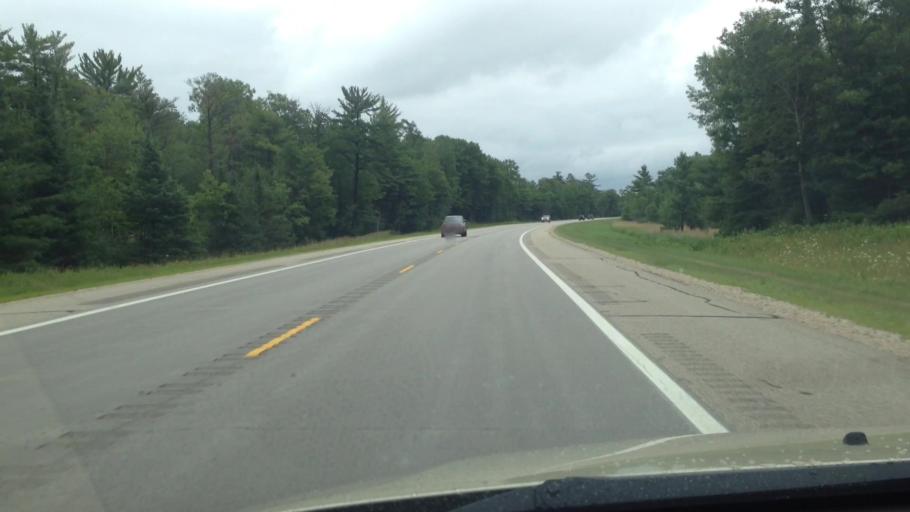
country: US
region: Michigan
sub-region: Schoolcraft County
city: Manistique
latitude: 45.9108
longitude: -86.4577
